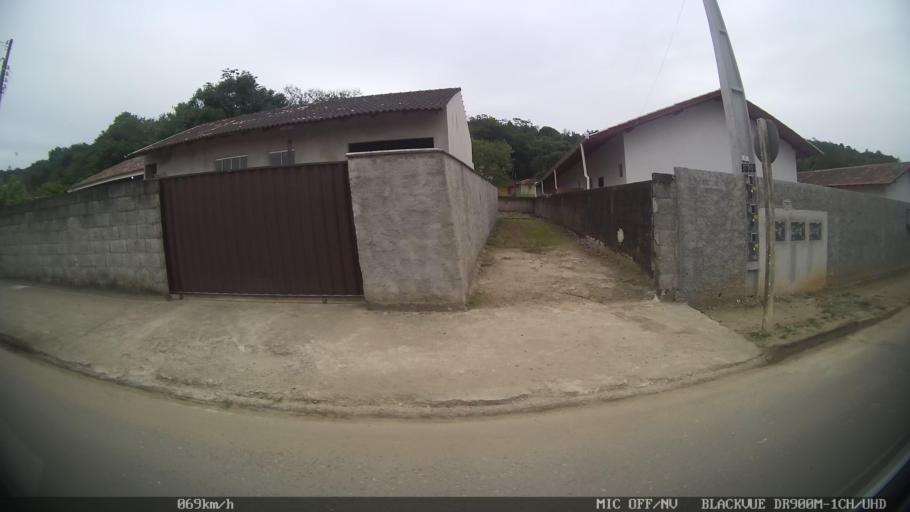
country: BR
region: Santa Catarina
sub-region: Joinville
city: Joinville
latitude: -26.3547
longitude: -48.7956
